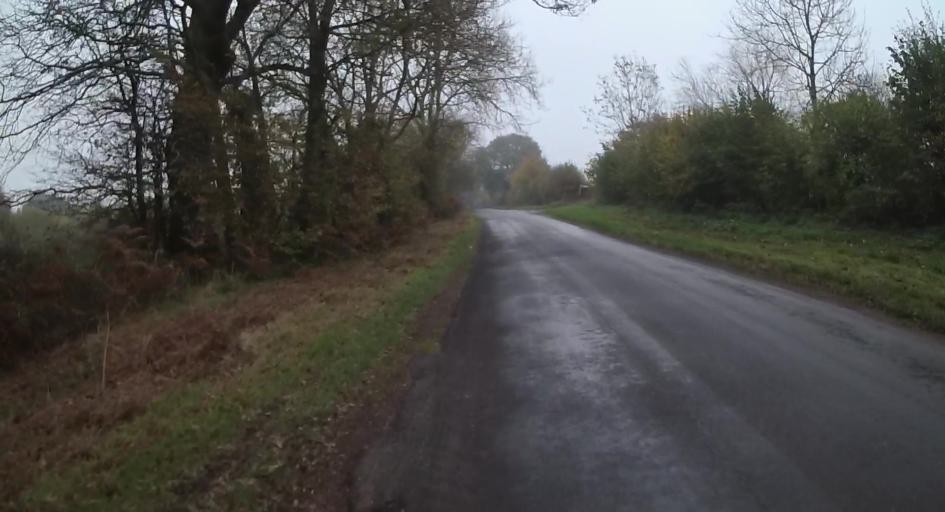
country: GB
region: England
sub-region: Hampshire
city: Long Sutton
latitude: 51.1968
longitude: -0.9506
